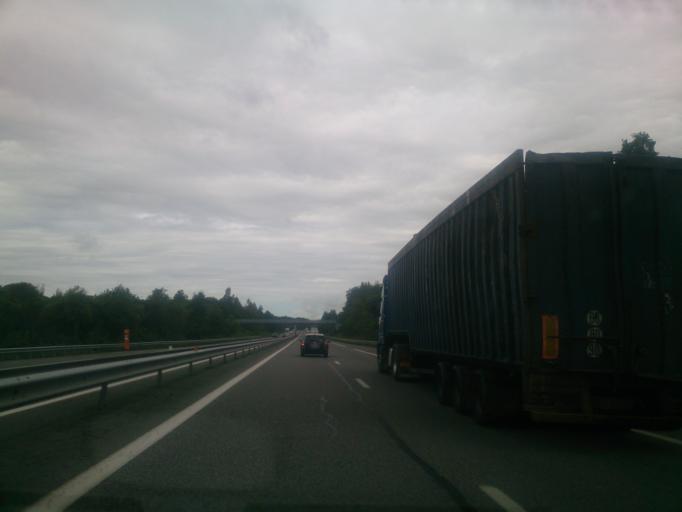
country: FR
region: Midi-Pyrenees
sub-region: Departement de la Haute-Garonne
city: Montrejeau
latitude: 43.1012
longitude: 0.4847
